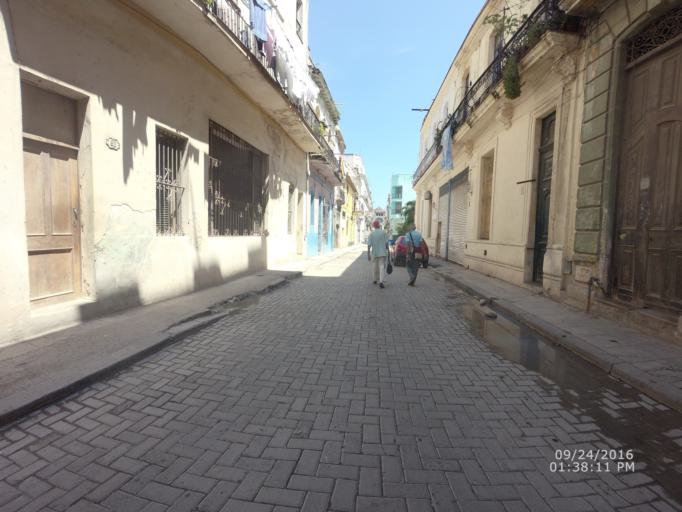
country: CU
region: La Habana
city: La Habana Vieja
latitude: 23.1351
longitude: -82.3494
